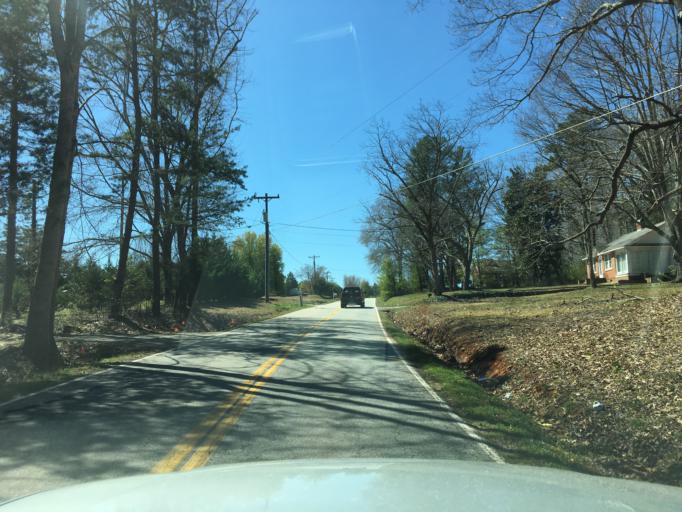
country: US
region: South Carolina
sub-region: Spartanburg County
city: Roebuck
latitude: 34.9032
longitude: -81.9600
